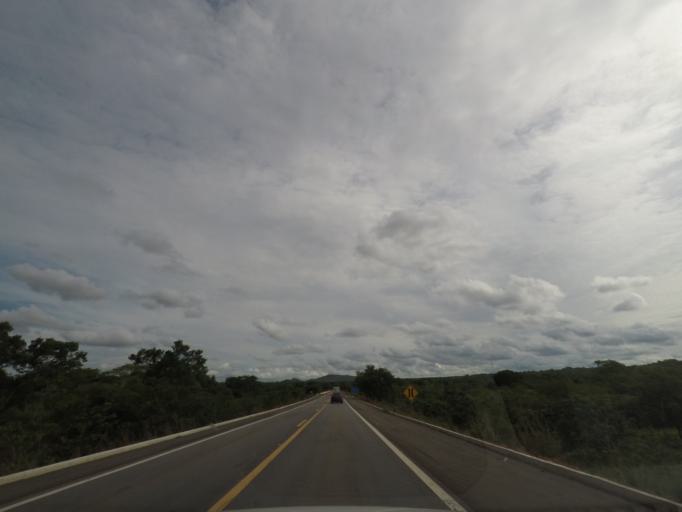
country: BR
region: Goias
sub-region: Uruacu
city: Uruacu
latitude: -14.7408
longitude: -49.0694
